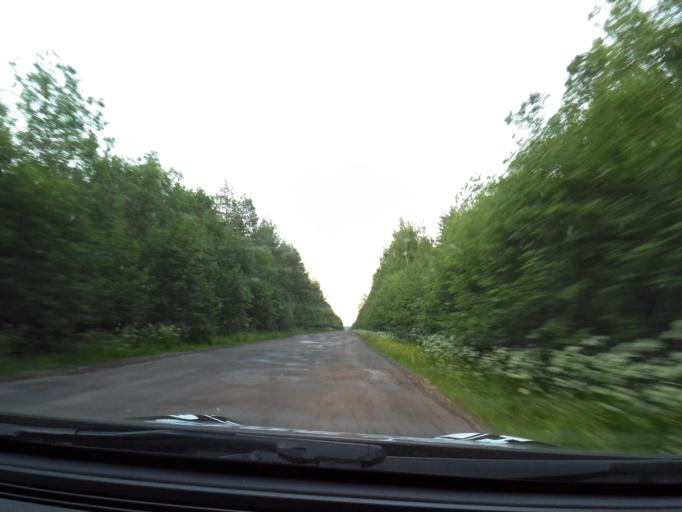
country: RU
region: Leningrad
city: Voznesen'ye
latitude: 60.8303
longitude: 35.6948
